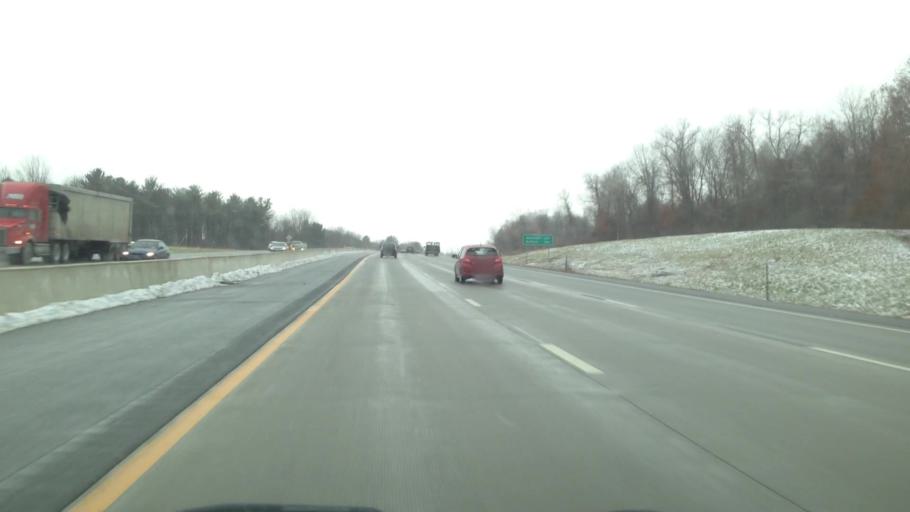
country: US
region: New York
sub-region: Albany County
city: Delmar
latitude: 42.6429
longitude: -73.8018
